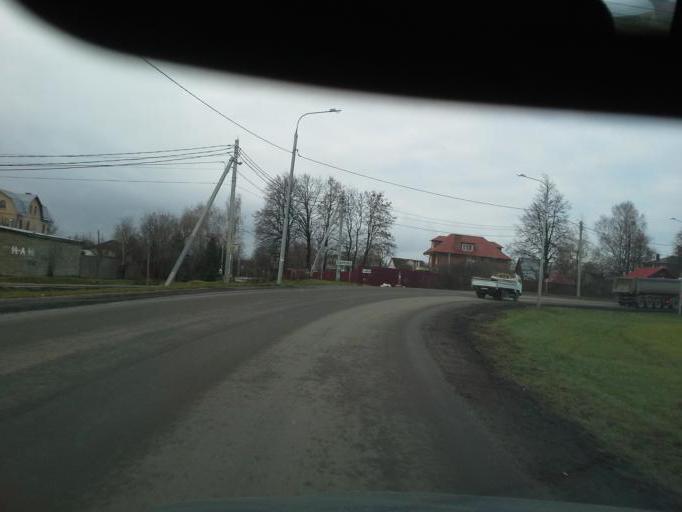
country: RU
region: Moskovskaya
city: Kommunarka
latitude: 55.5586
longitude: 37.4199
